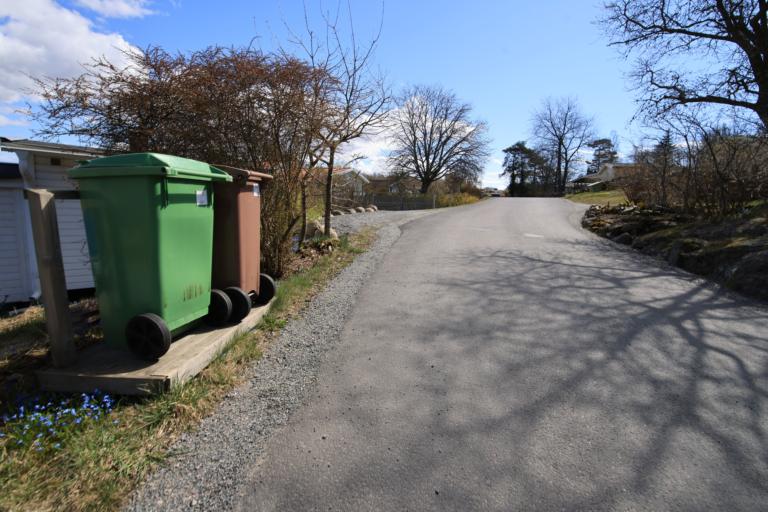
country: SE
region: Halland
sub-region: Varbergs Kommun
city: Varberg
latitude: 57.1835
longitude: 12.2378
